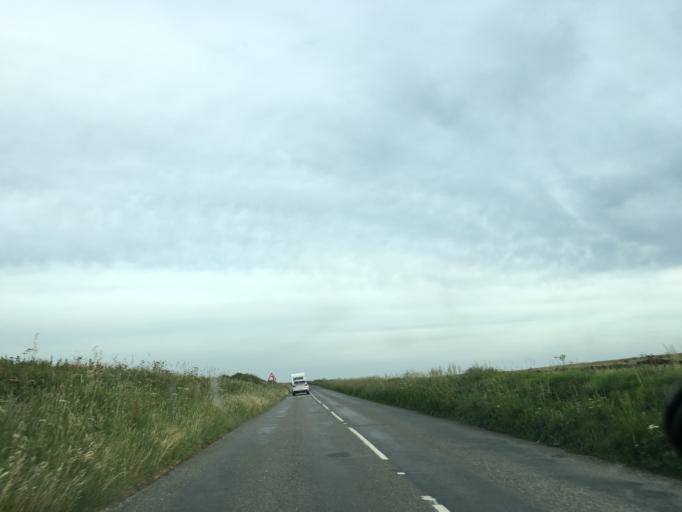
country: GB
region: England
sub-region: Isle of Wight
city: Shalfleet
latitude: 50.6412
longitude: -1.4281
